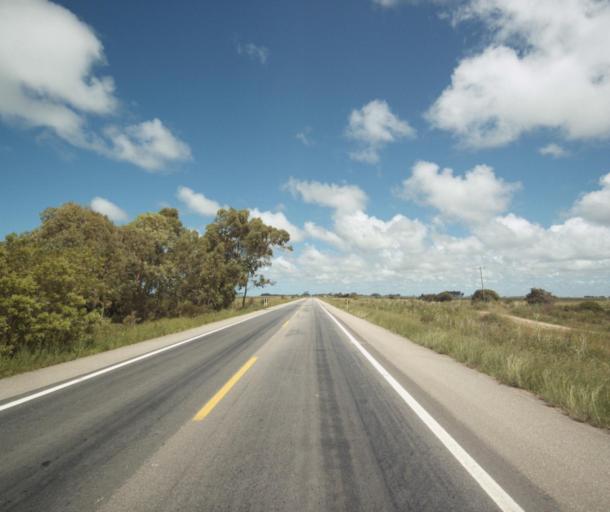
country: UY
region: Cerro Largo
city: Rio Branco
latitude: -32.8578
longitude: -52.7061
